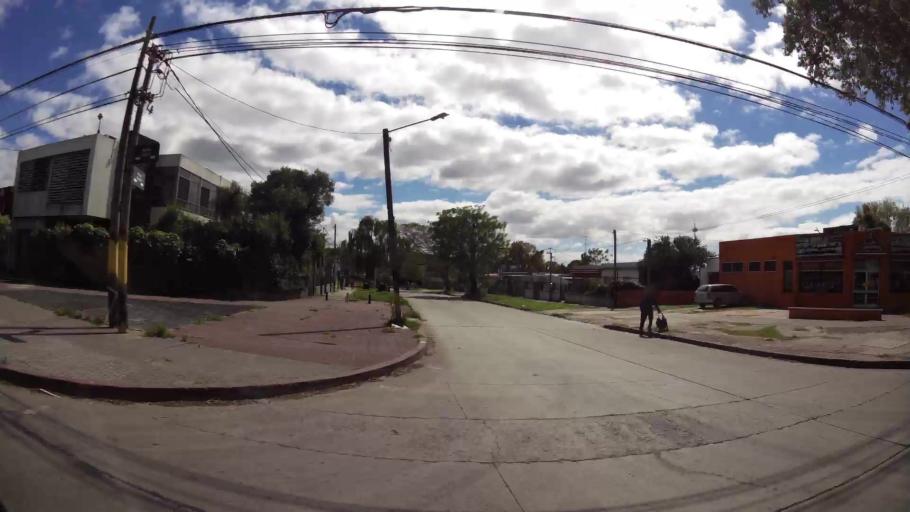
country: UY
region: Canelones
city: Paso de Carrasco
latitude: -34.8724
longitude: -56.1150
